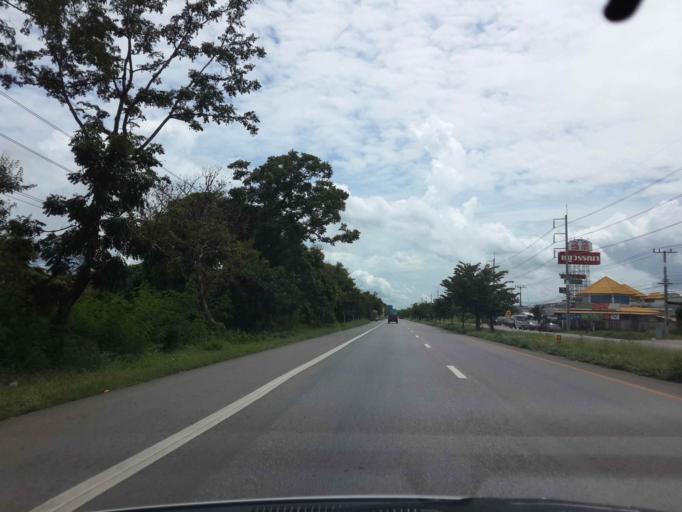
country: TH
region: Ratchaburi
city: Pak Tho
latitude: 13.3760
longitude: 99.8211
